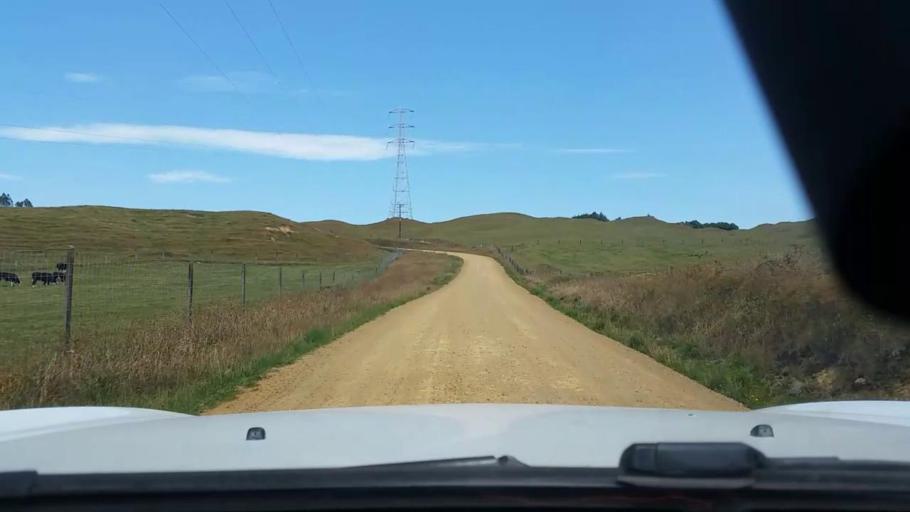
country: NZ
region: Bay of Plenty
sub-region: Rotorua District
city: Rotorua
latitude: -38.0061
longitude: 176.2001
